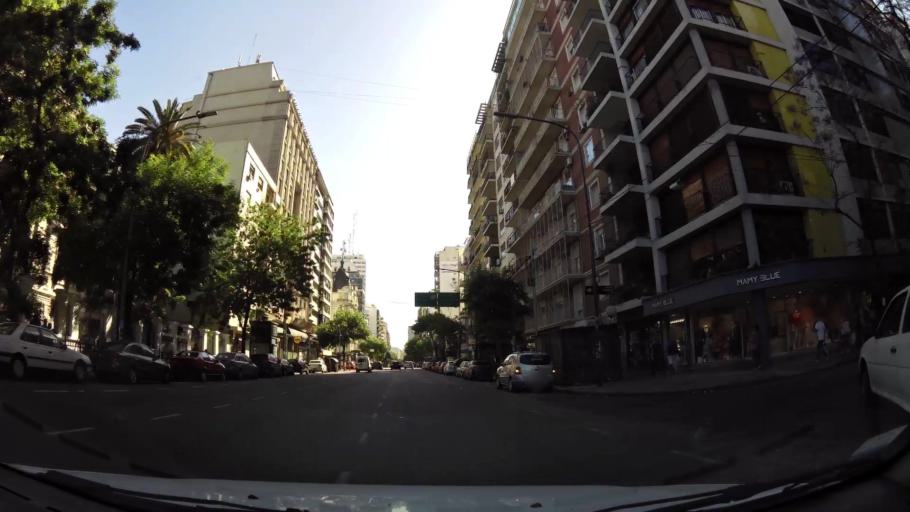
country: AR
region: Buenos Aires F.D.
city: Villa Santa Rita
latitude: -34.6178
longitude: -58.4353
